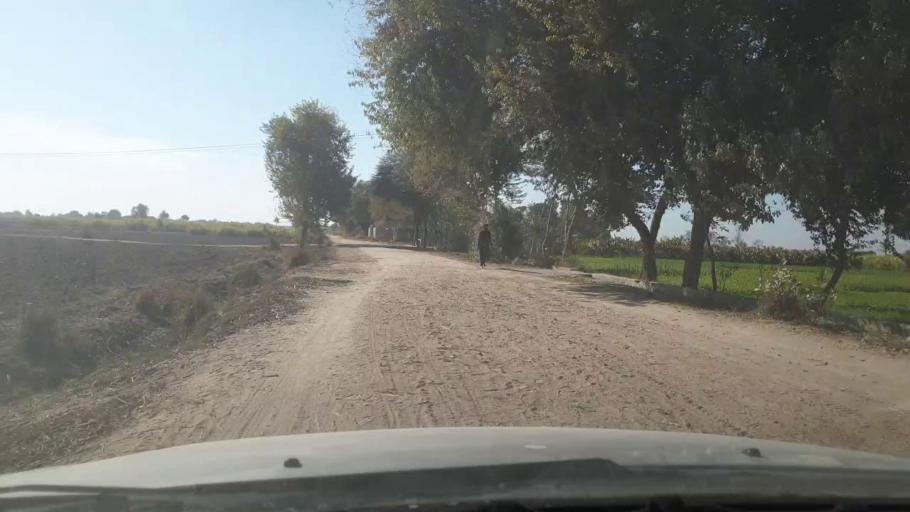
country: PK
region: Sindh
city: Ghotki
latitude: 27.9790
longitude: 69.1991
